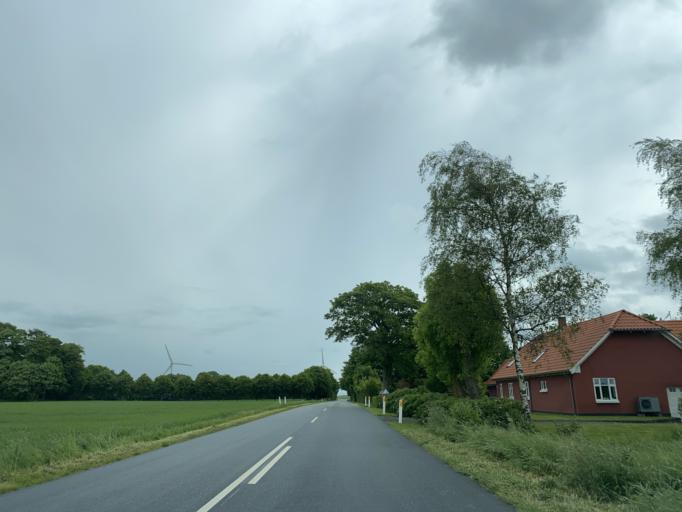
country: DK
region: Central Jutland
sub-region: Arhus Kommune
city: Sabro
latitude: 56.2541
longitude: 9.9714
